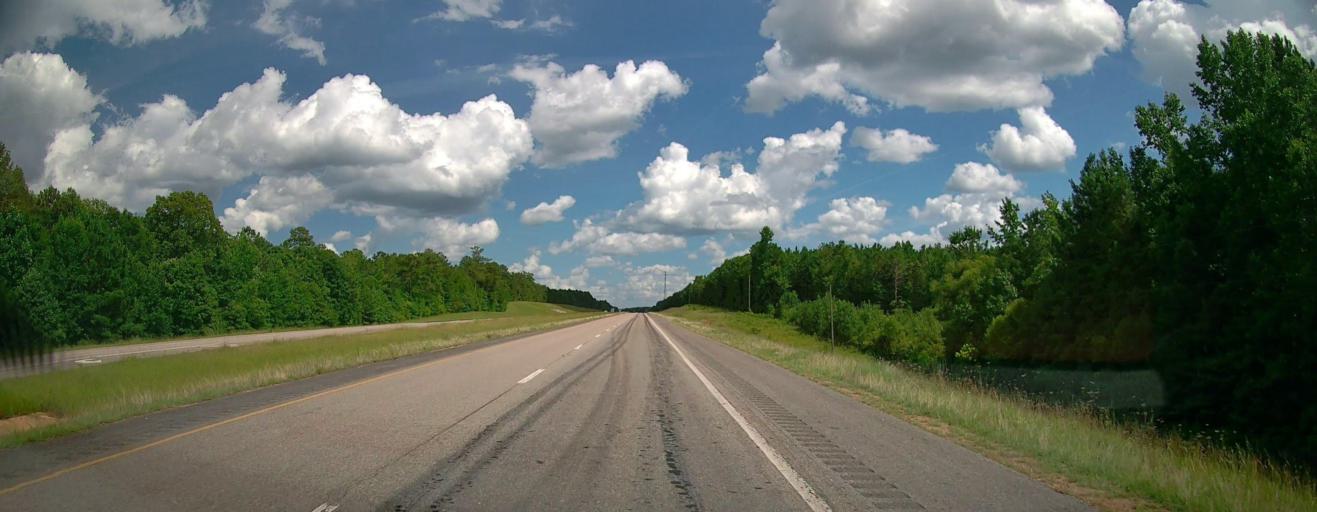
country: US
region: Mississippi
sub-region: Lowndes County
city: New Hope
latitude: 33.4582
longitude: -88.2220
